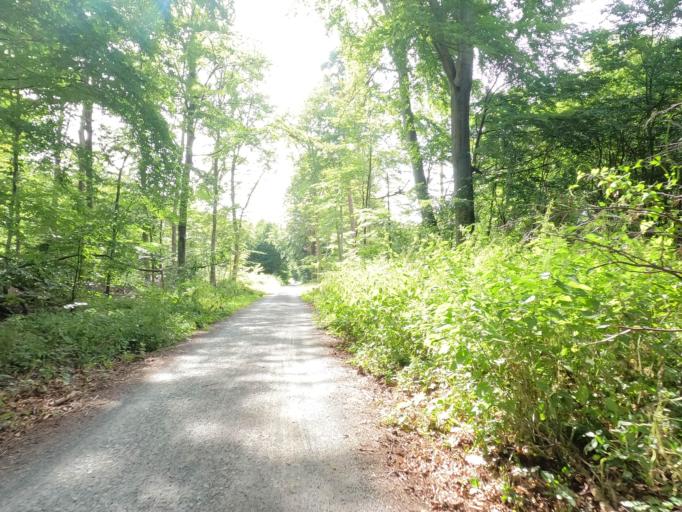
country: DE
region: Hesse
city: Langen
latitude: 50.0180
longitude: 8.6447
